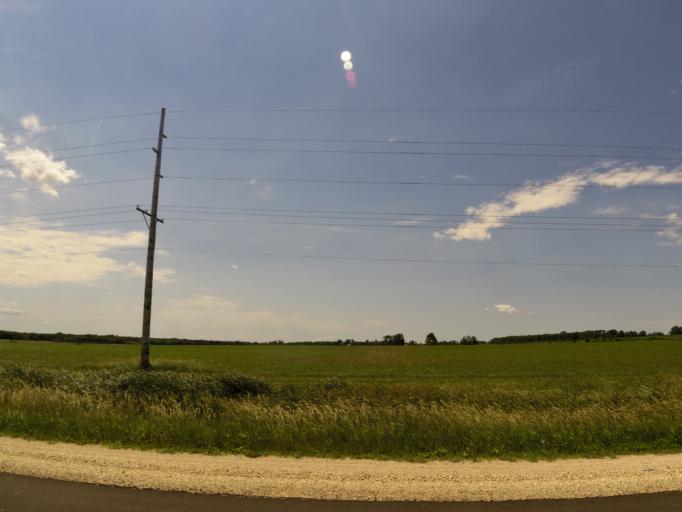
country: US
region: Iowa
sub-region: Bremer County
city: Tripoli
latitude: 42.7148
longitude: -92.1889
